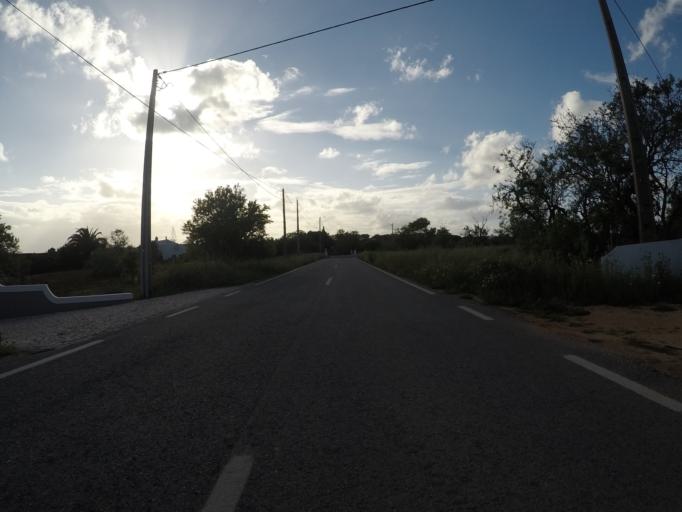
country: PT
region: Faro
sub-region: Lagoa
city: Carvoeiro
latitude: 37.0938
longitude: -8.4332
